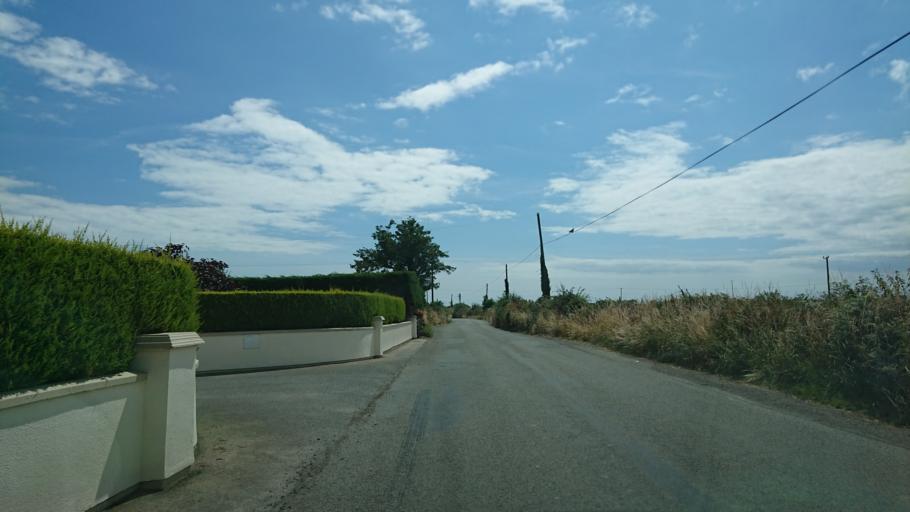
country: IE
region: Munster
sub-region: Waterford
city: Portlaw
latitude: 52.1867
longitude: -7.3326
